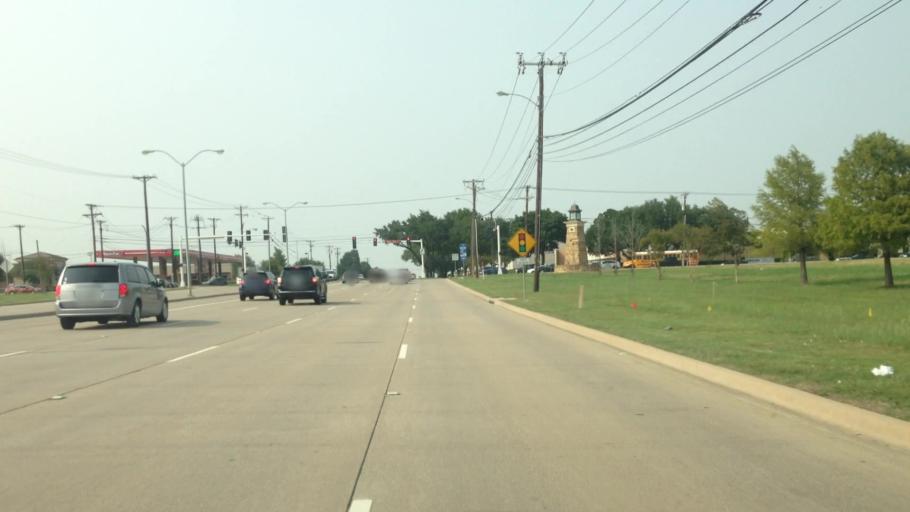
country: US
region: Texas
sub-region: Dallas County
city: Farmers Branch
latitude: 32.9166
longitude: -96.9249
